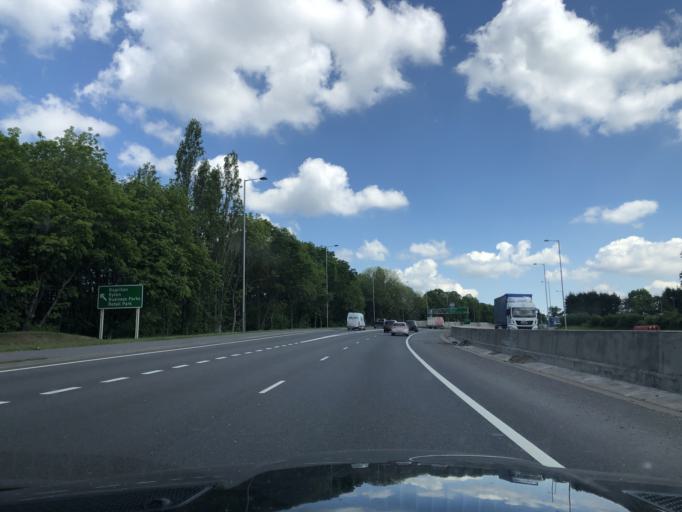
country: GB
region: England
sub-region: Warwickshire
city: Ryton on Dunsmore
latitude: 52.3788
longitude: -1.4753
